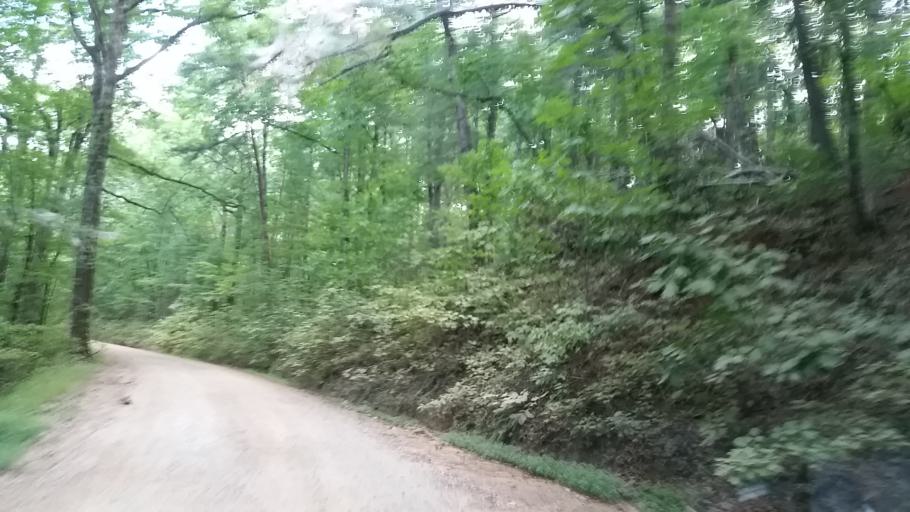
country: US
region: Georgia
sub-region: Lumpkin County
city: Dahlonega
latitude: 34.6325
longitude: -84.1005
